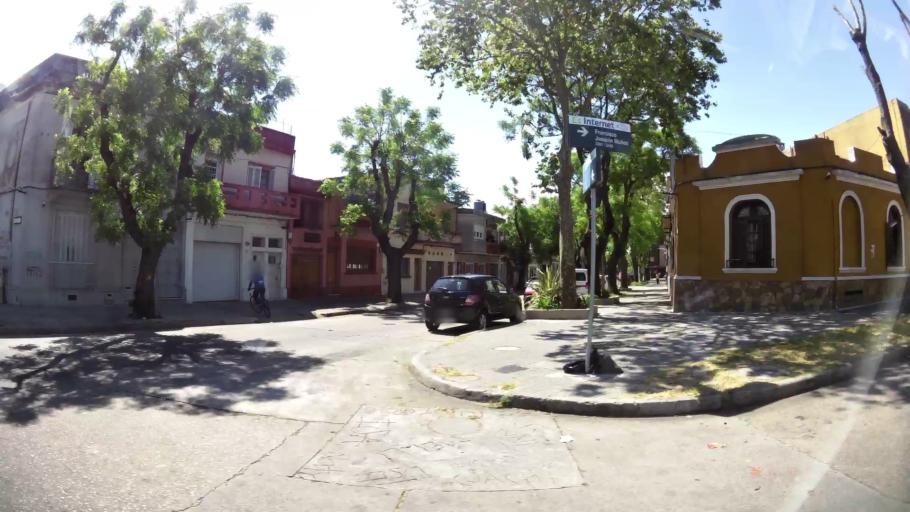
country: UY
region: Montevideo
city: Montevideo
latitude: -34.9034
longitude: -56.1431
